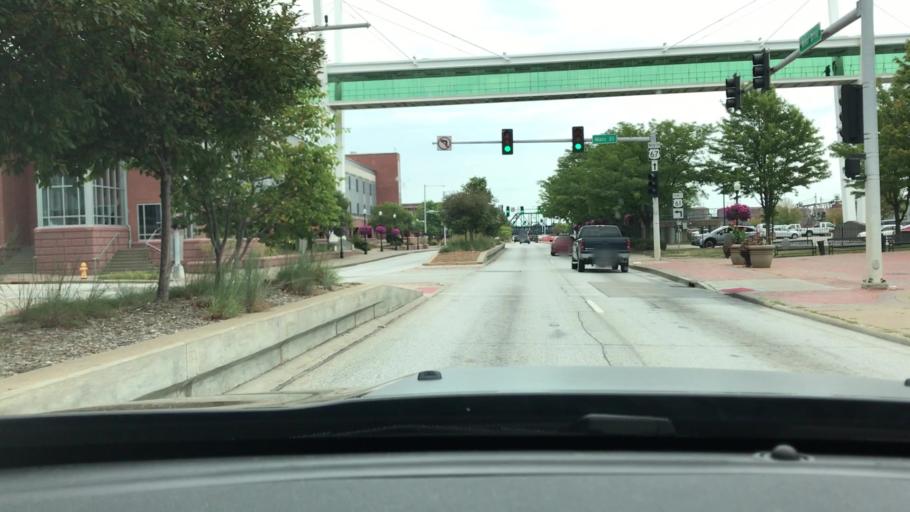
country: US
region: Iowa
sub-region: Scott County
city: Davenport
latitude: 41.5202
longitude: -90.5760
